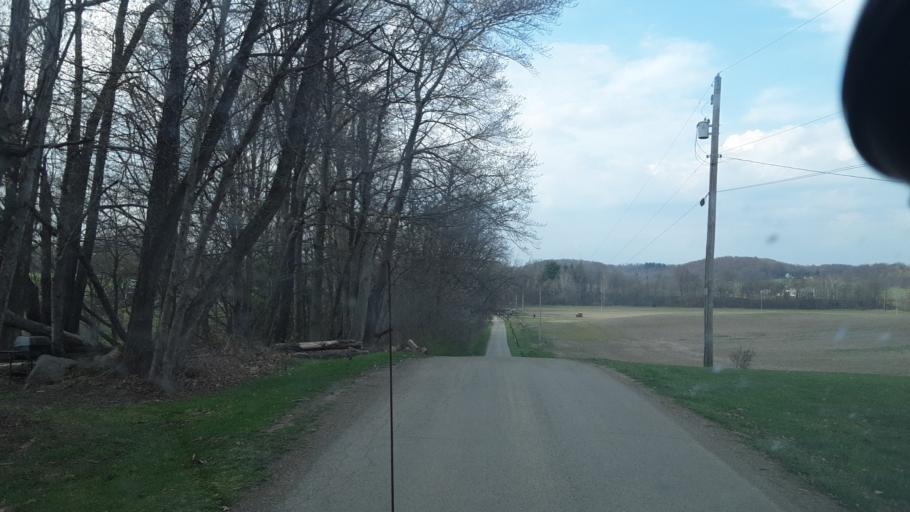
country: US
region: Ohio
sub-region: Richland County
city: Lincoln Heights
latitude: 40.7272
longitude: -82.4258
